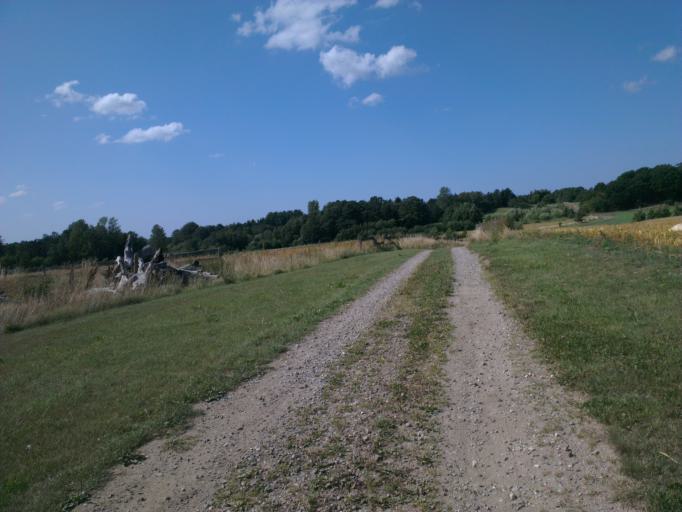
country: DK
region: Capital Region
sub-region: Frederikssund Kommune
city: Frederikssund
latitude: 55.8794
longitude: 12.0802
